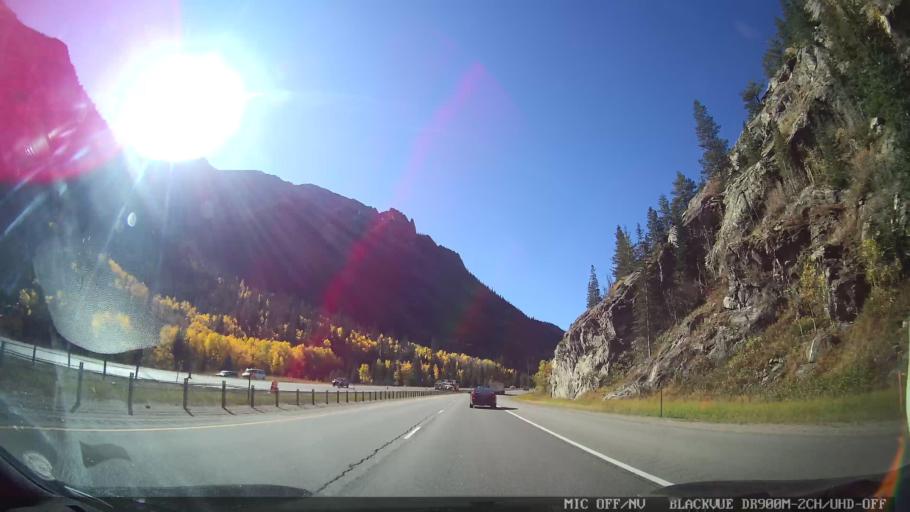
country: US
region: Colorado
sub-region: Summit County
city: Frisco
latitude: 39.5604
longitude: -106.1300
